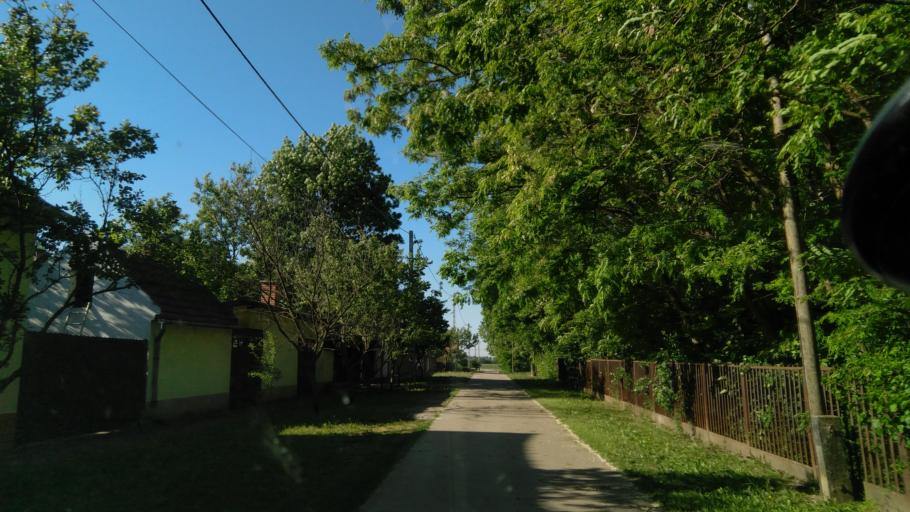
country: HU
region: Bekes
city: Elek
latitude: 46.5311
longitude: 21.2326
